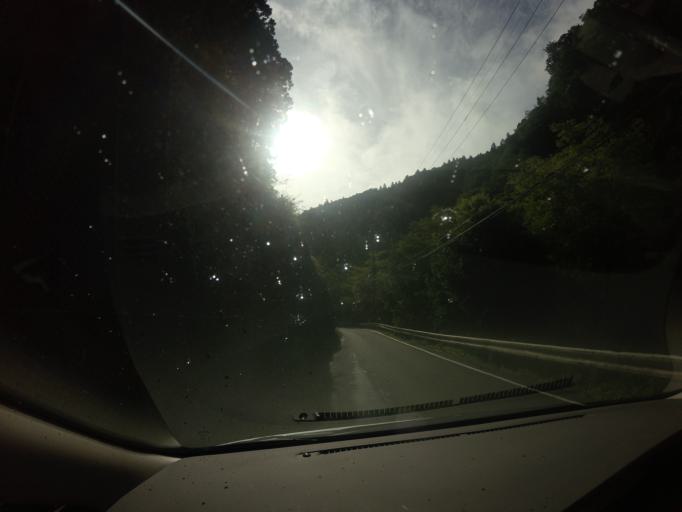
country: JP
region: Wakayama
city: Shingu
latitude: 33.9684
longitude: 135.8161
